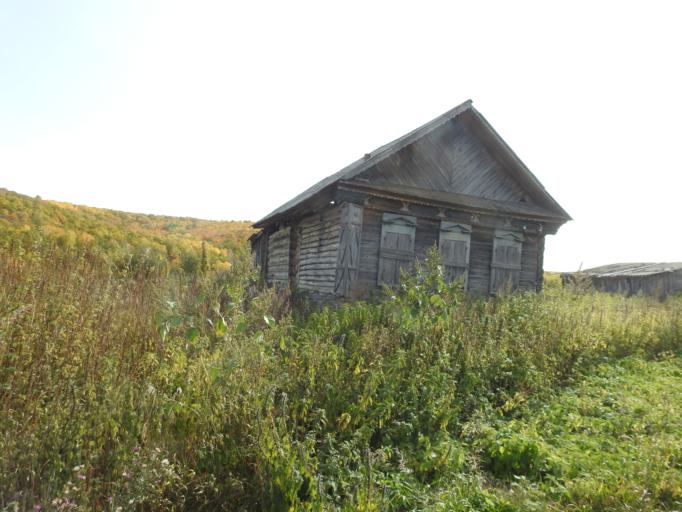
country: RU
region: Saratov
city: Baltay
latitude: 52.5172
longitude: 46.6829
